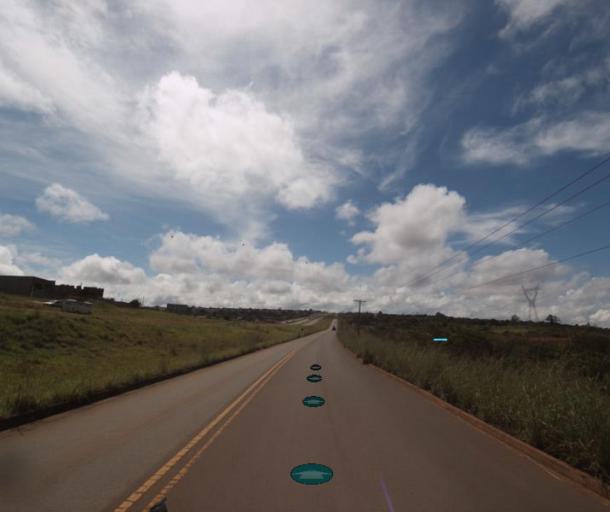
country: BR
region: Federal District
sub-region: Brasilia
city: Brasilia
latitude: -15.7412
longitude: -48.3115
